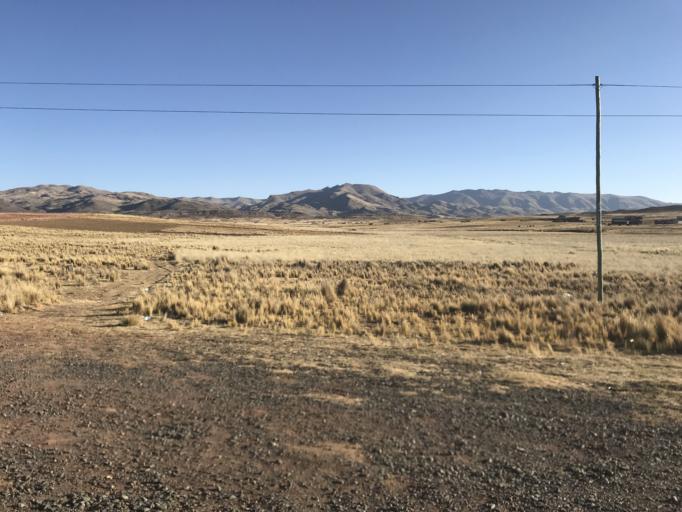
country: BO
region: La Paz
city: Tiahuanaco
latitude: -16.5662
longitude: -68.6182
